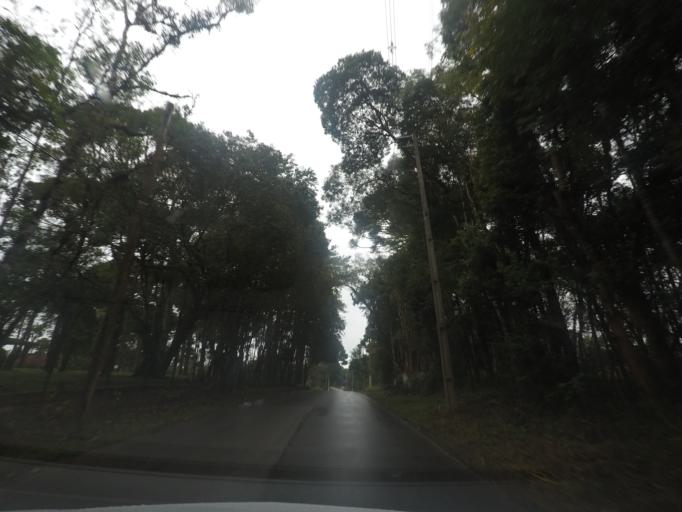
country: BR
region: Parana
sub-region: Colombo
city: Colombo
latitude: -25.3077
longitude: -49.1418
